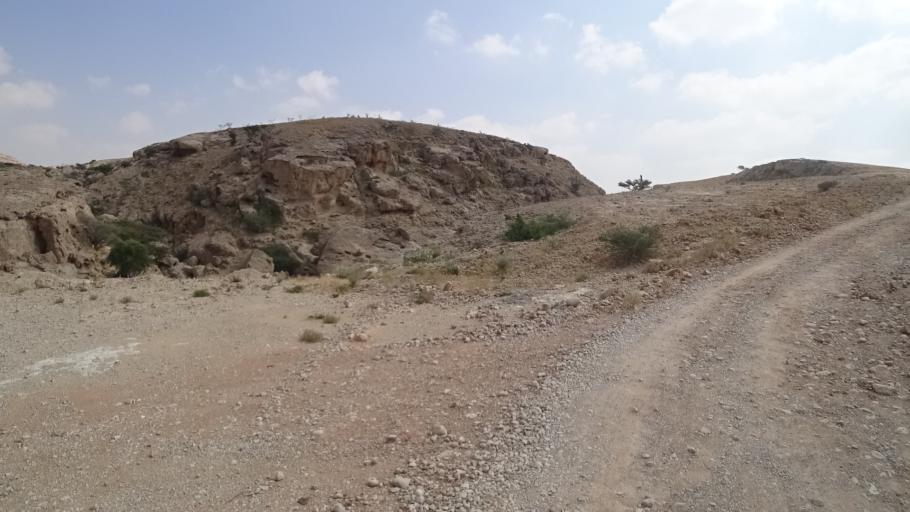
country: OM
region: Zufar
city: Salalah
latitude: 17.2464
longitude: 53.8891
